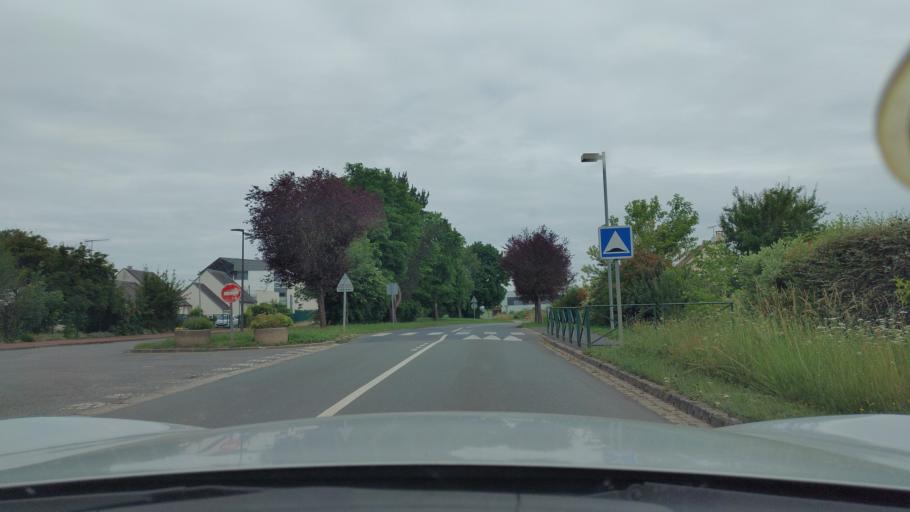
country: FR
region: Picardie
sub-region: Departement de l'Oise
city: Betz
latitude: 49.1592
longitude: 2.9500
